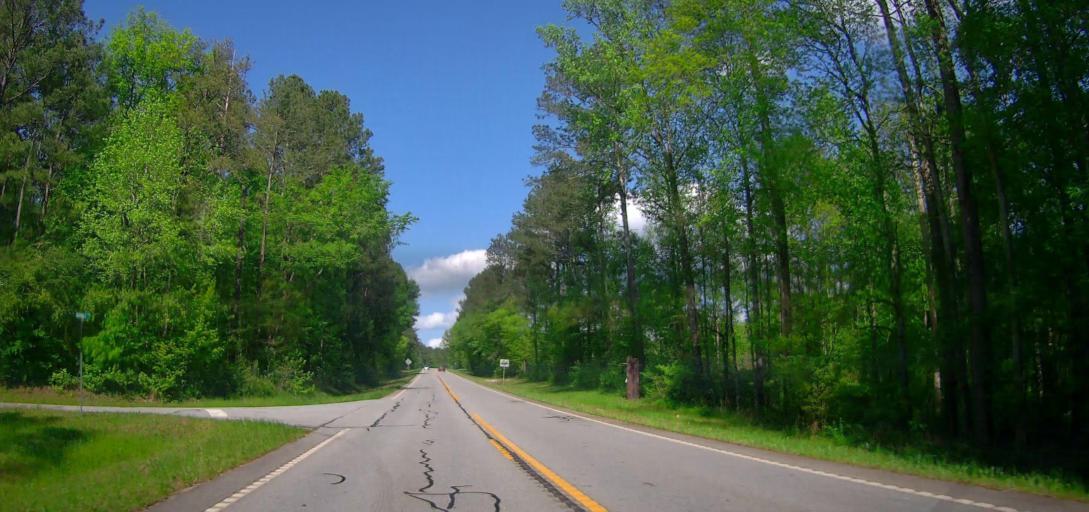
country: US
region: Georgia
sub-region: Morgan County
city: Madison
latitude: 33.6145
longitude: -83.3346
